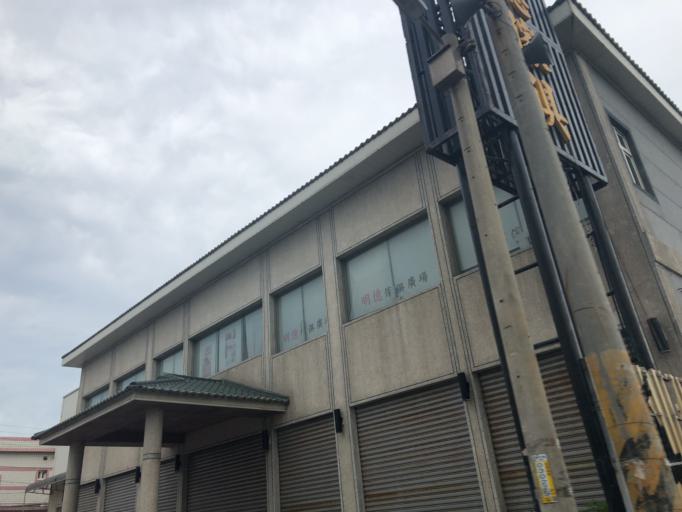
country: TW
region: Taiwan
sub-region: Chiayi
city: Taibao
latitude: 23.7093
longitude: 120.2007
